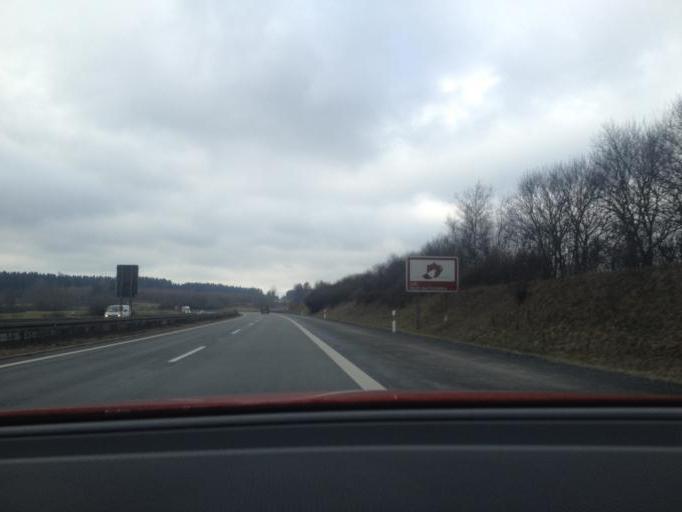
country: DE
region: Bavaria
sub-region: Upper Franconia
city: Schonwald
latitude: 50.2010
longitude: 12.1048
